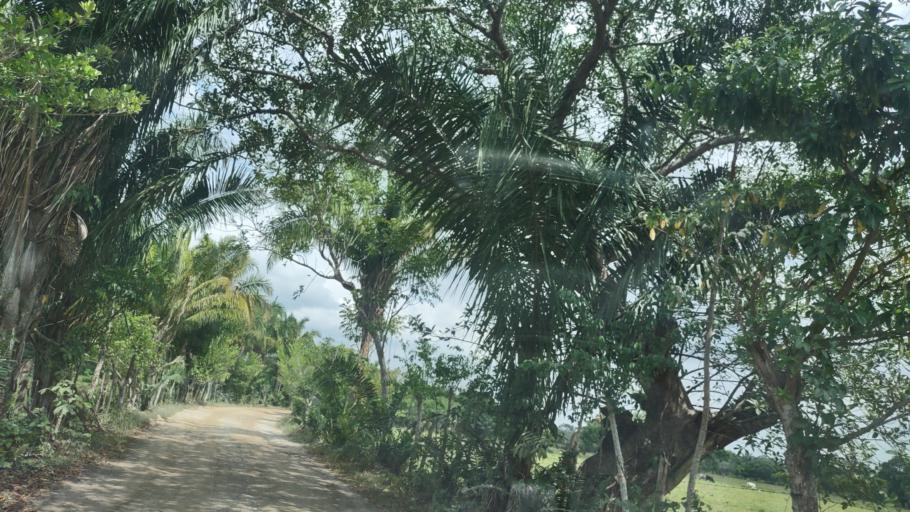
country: MX
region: Veracruz
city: Las Choapas
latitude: 17.9623
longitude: -94.1229
